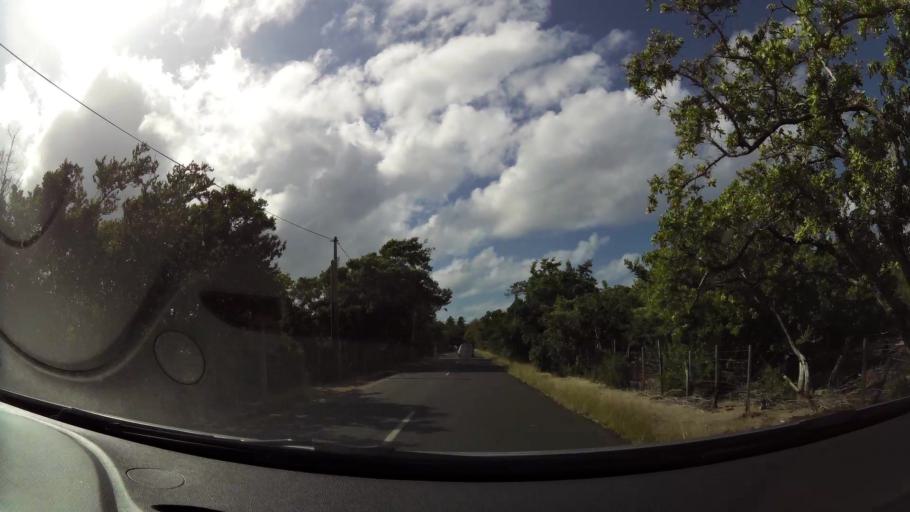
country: MQ
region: Martinique
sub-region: Martinique
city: Le Marin
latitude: 14.4043
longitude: -60.8766
